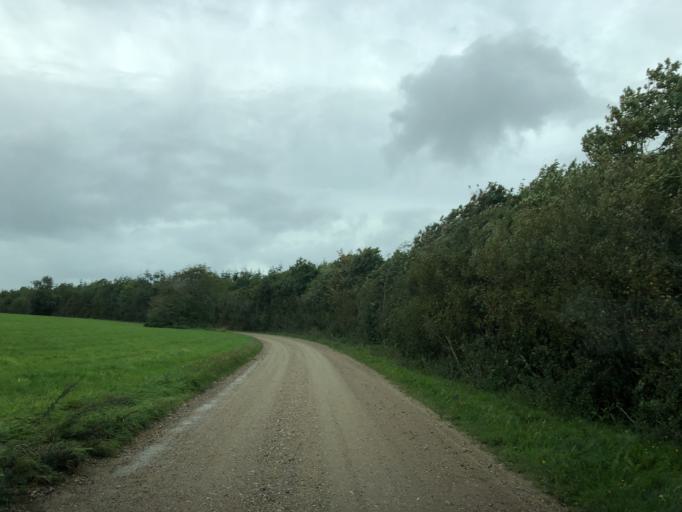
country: DK
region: Central Jutland
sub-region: Holstebro Kommune
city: Holstebro
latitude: 56.2357
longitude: 8.5255
